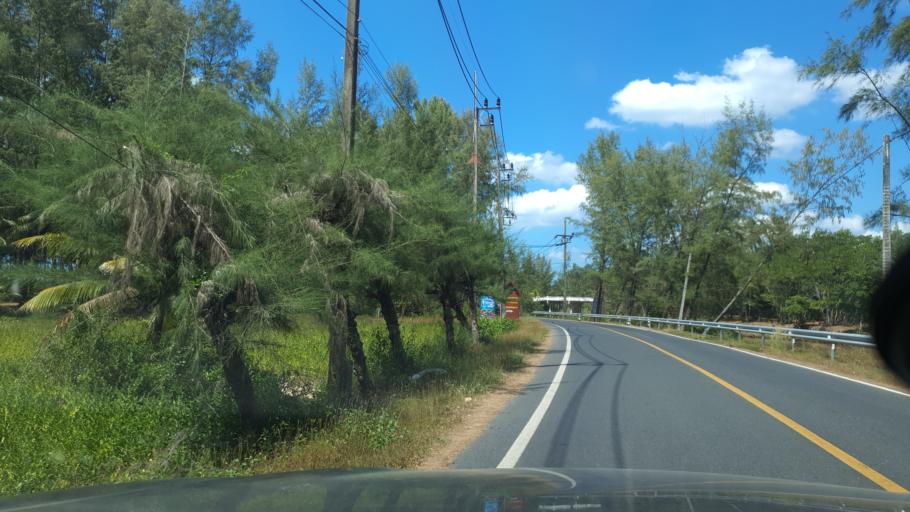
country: TH
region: Phangnga
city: Thai Mueang
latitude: 8.2926
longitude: 98.2738
